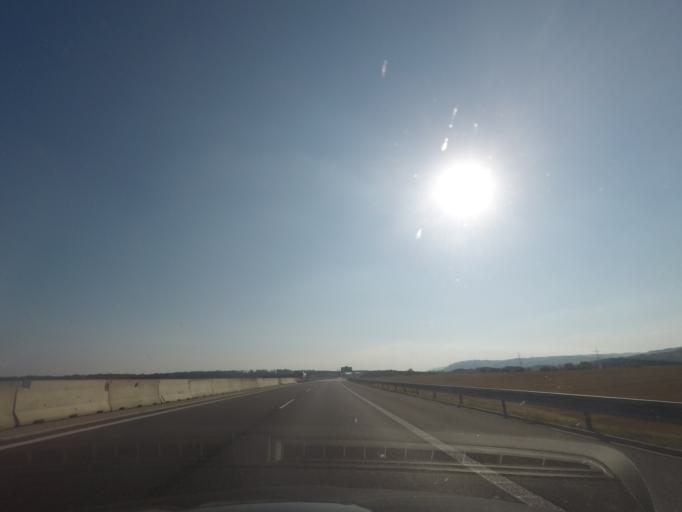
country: CZ
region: Olomoucky
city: Belotin
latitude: 49.5909
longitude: 17.7789
